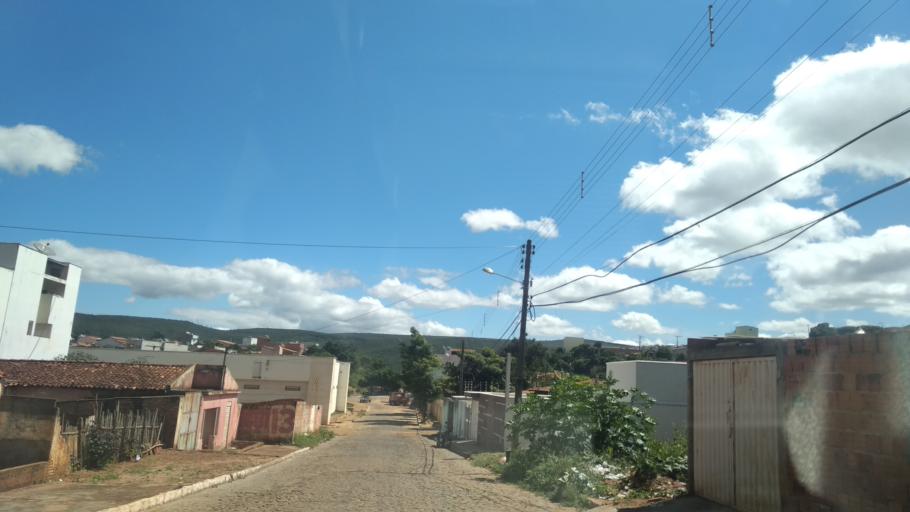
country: BR
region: Bahia
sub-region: Caetite
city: Caetite
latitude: -14.0610
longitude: -42.4845
